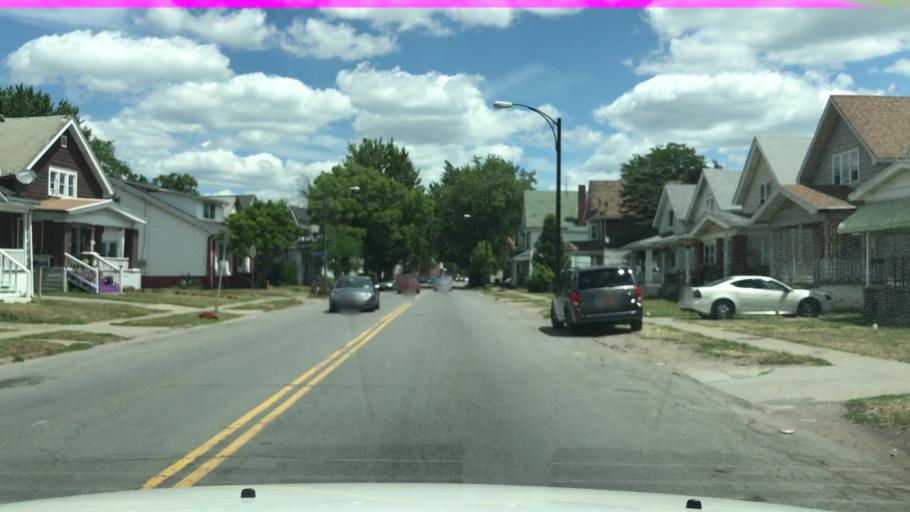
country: US
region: New York
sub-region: Erie County
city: Sloan
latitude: 42.9065
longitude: -78.8013
